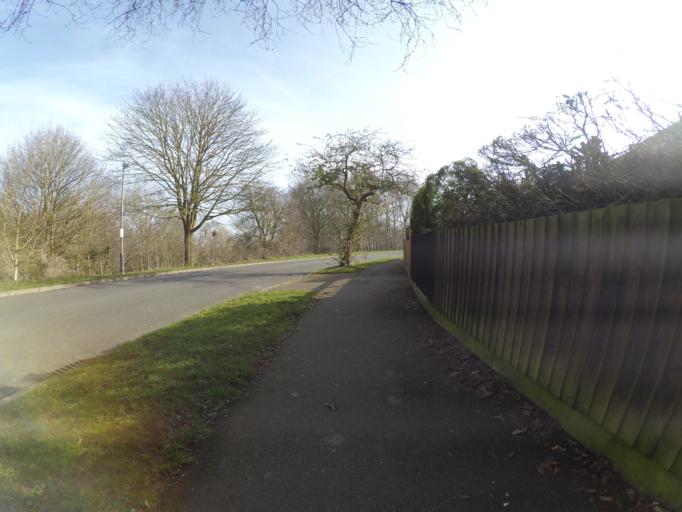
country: GB
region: England
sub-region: Warwickshire
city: Rugby
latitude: 52.3668
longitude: -1.2270
